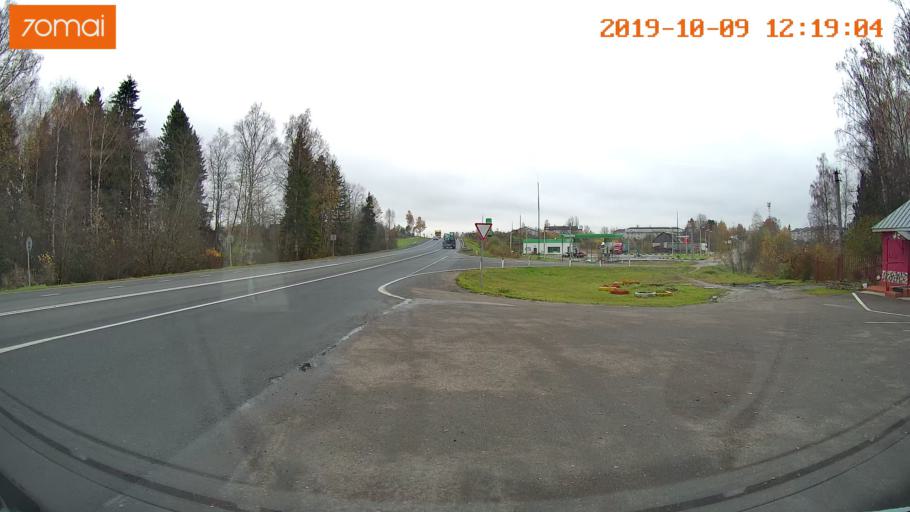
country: RU
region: Jaroslavl
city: Prechistoye
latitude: 58.4361
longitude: 40.3215
